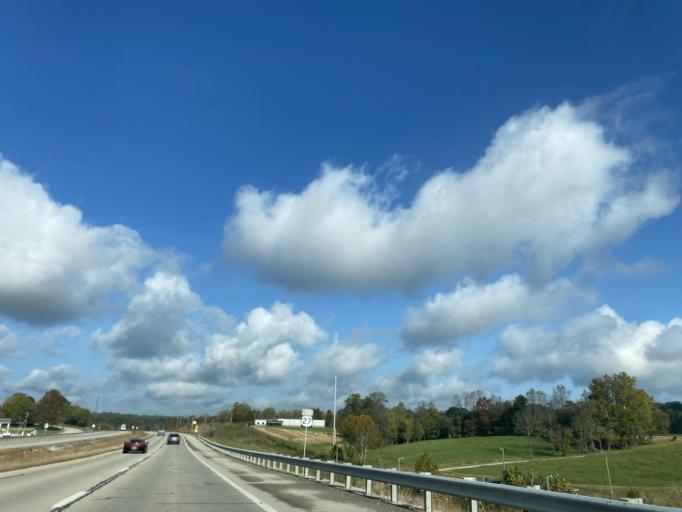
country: US
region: Kentucky
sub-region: Campbell County
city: Claryville
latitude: 38.8539
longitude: -84.3836
